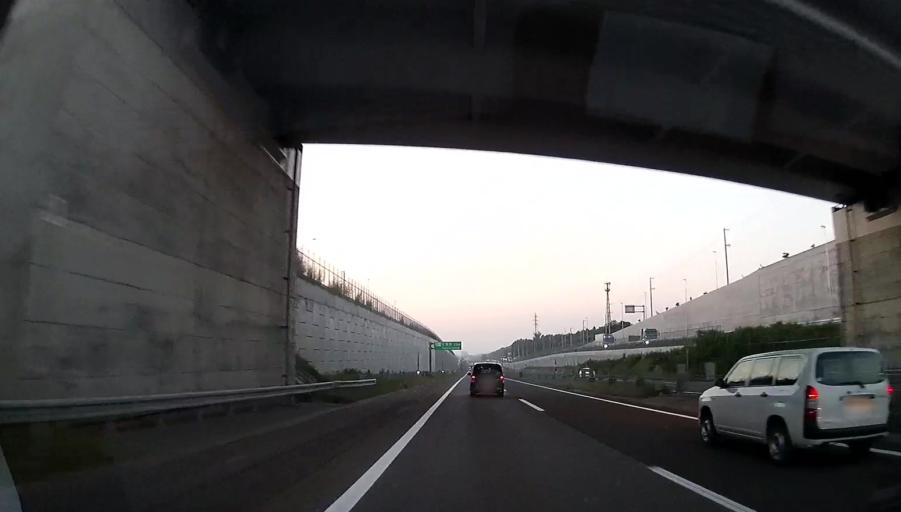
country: JP
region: Hokkaido
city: Kitahiroshima
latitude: 42.9924
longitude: 141.4692
